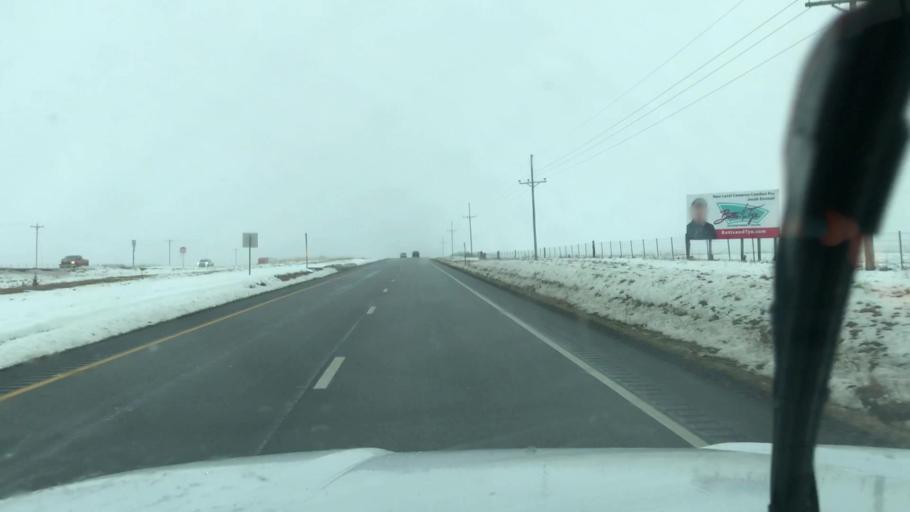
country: US
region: Missouri
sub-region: Clinton County
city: Cameron
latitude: 39.7538
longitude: -94.2780
